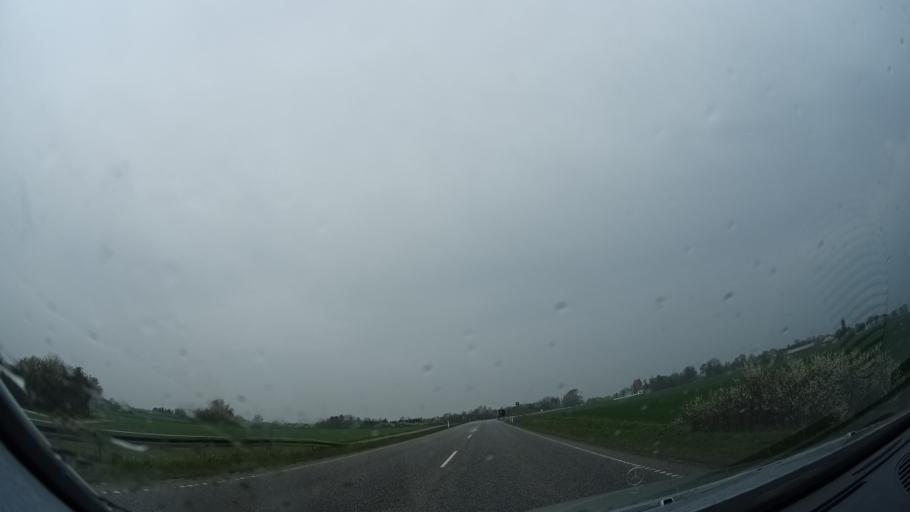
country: DK
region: Zealand
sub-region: Holbaek Kommune
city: Holbaek
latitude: 55.7405
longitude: 11.6226
